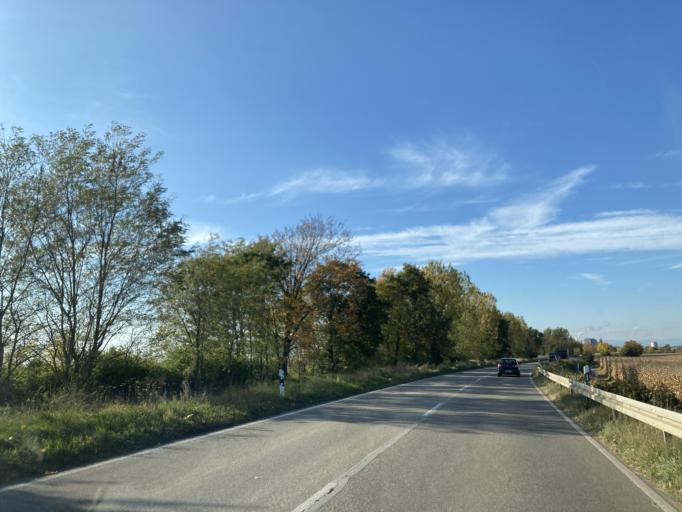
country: DE
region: Baden-Wuerttemberg
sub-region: Freiburg Region
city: Eschbach
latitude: 47.8826
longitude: 7.6356
